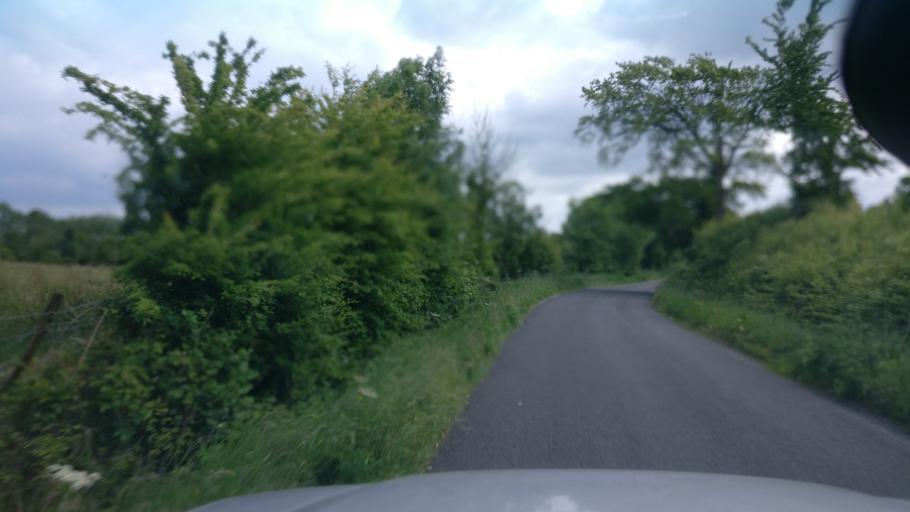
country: IE
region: Connaught
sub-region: County Galway
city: Ballinasloe
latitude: 53.2840
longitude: -8.3394
